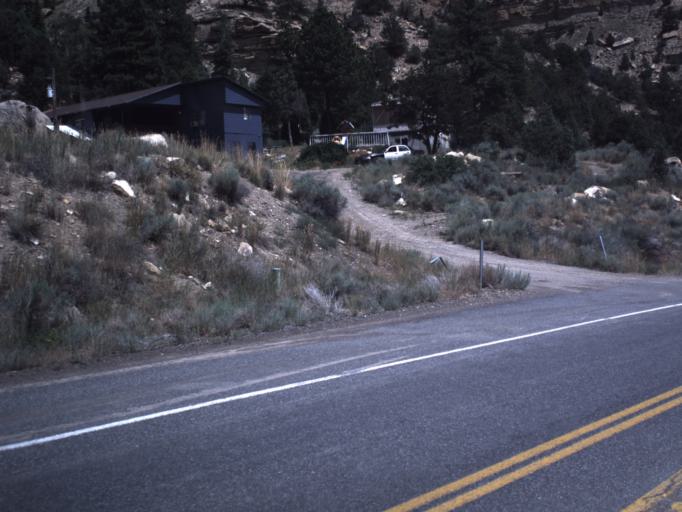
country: US
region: Utah
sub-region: Emery County
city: Huntington
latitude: 39.4151
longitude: -111.1179
